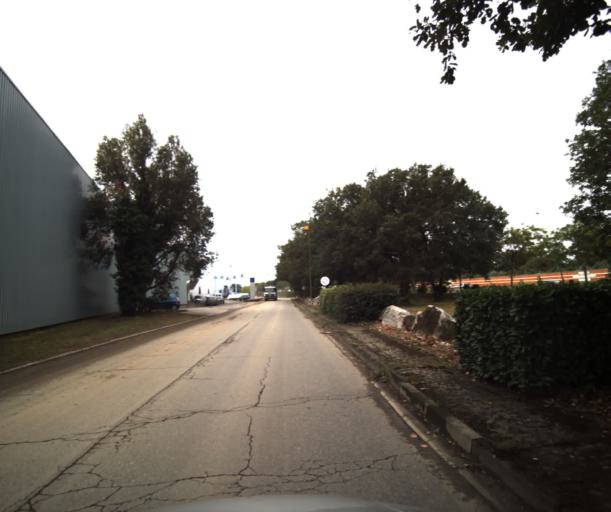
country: FR
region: Midi-Pyrenees
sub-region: Departement de la Haute-Garonne
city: Portet-sur-Garonne
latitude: 43.5500
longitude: 1.4068
